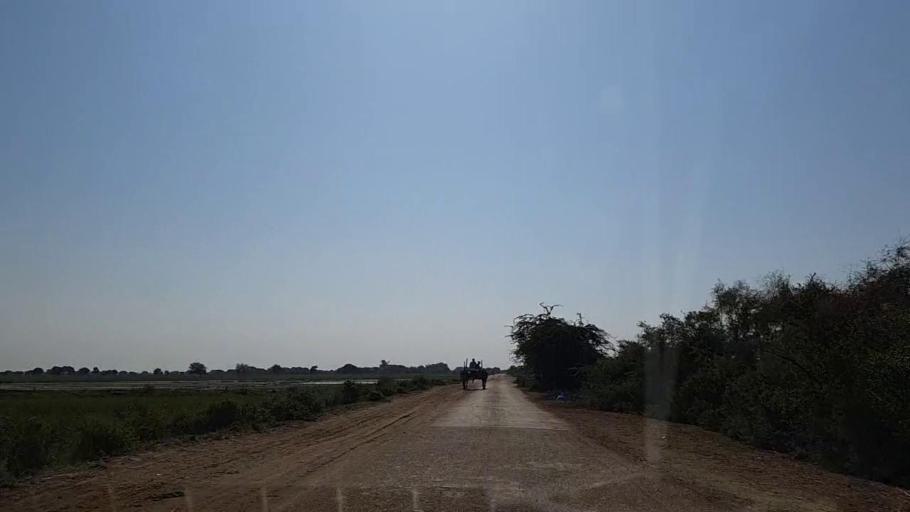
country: PK
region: Sindh
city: Chuhar Jamali
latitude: 24.5205
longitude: 68.0936
